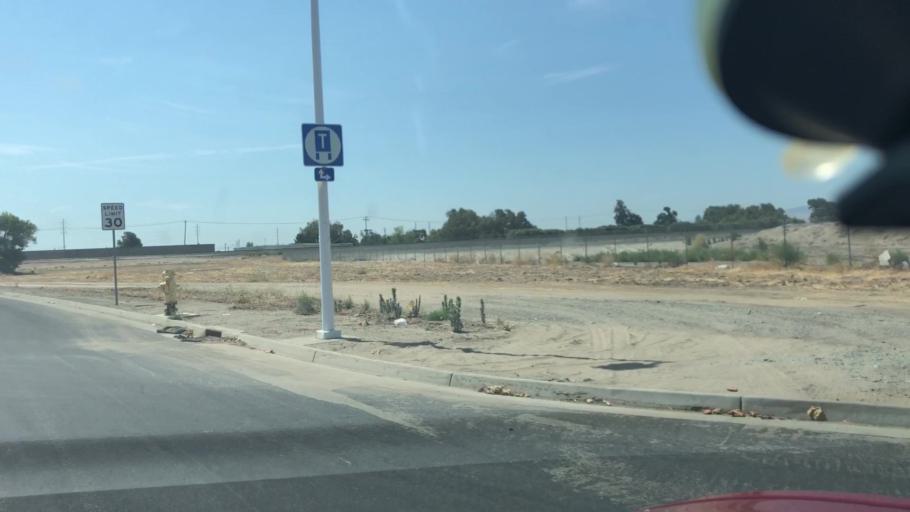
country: US
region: California
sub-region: San Joaquin County
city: Lathrop
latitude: 37.7984
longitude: -121.2821
